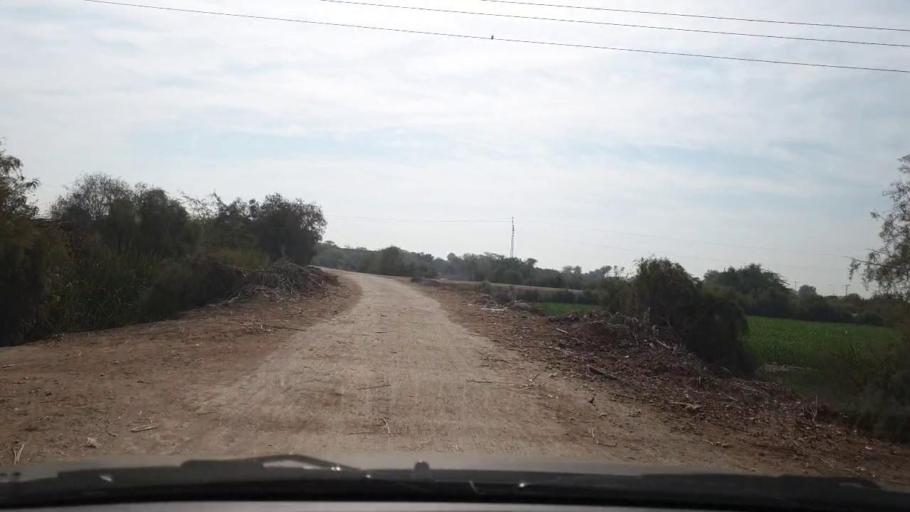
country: PK
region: Sindh
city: Shahpur Chakar
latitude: 26.1737
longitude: 68.6793
